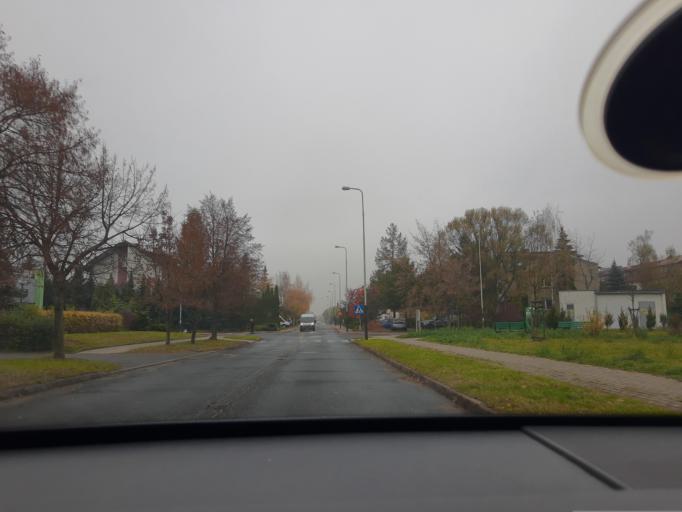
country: PL
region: Lodz Voivodeship
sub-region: Powiat pabianicki
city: Konstantynow Lodzki
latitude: 51.7425
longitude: 19.3785
